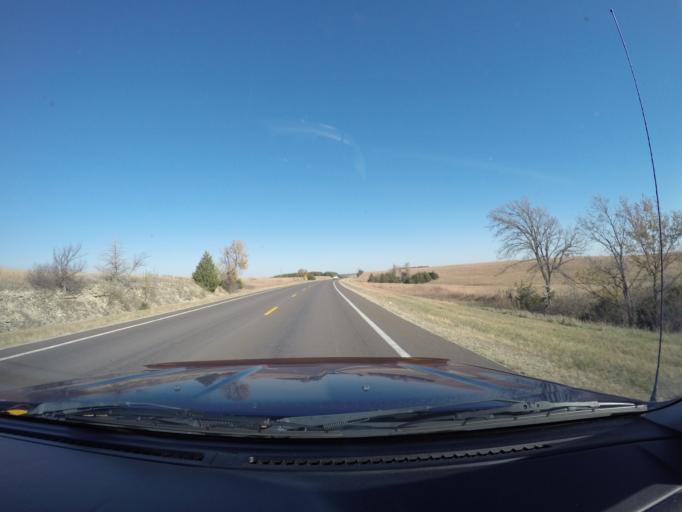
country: US
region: Kansas
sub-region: Marshall County
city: Blue Rapids
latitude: 39.4533
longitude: -96.7636
